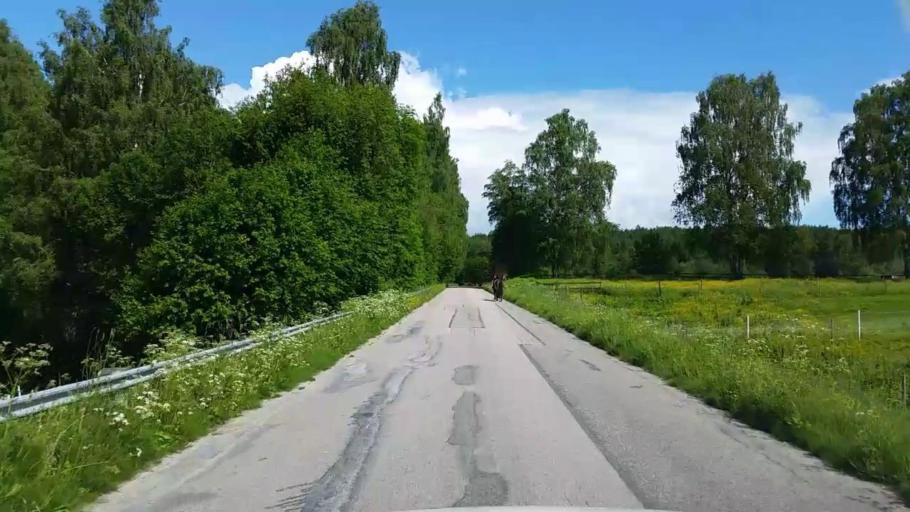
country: SE
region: Vaestmanland
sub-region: Fagersta Kommun
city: Fagersta
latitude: 59.9767
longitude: 15.7437
